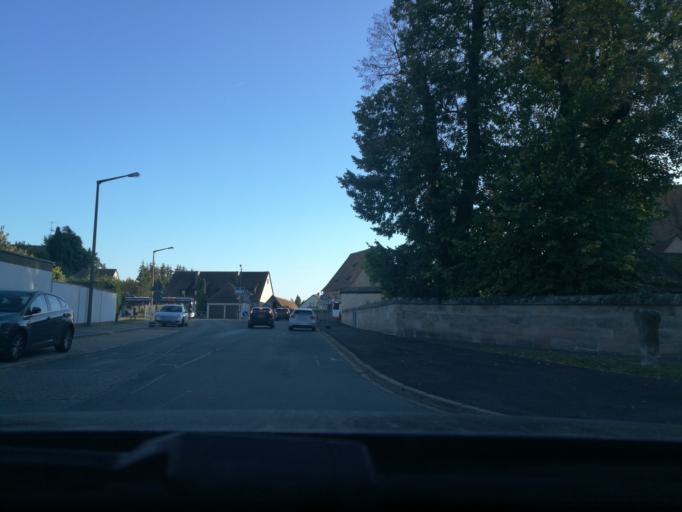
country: DE
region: Bavaria
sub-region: Regierungsbezirk Mittelfranken
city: Furth
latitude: 49.5308
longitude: 11.0117
